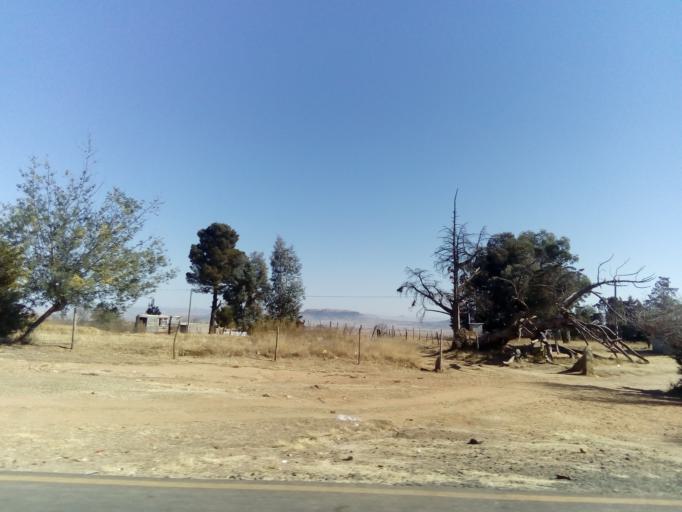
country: LS
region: Berea
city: Teyateyaneng
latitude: -29.1166
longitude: 27.8234
